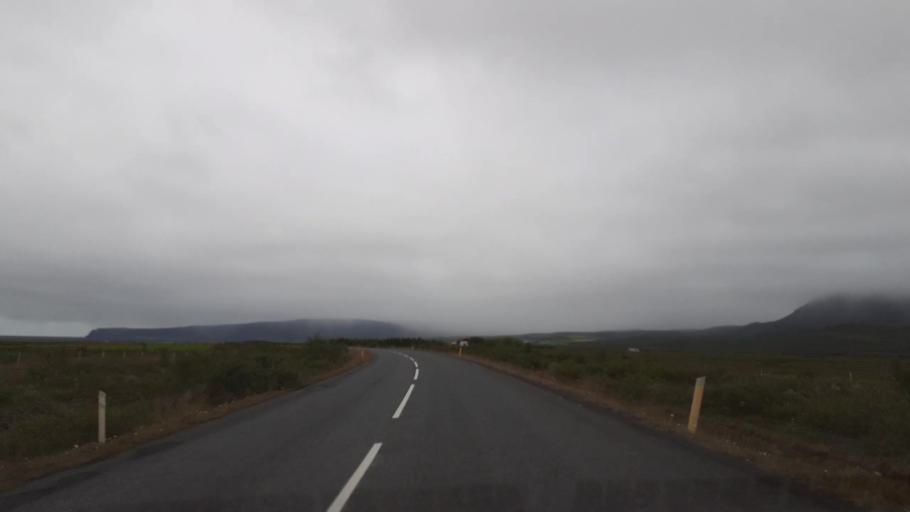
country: IS
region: Northeast
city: Husavik
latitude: 66.0785
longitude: -16.4302
